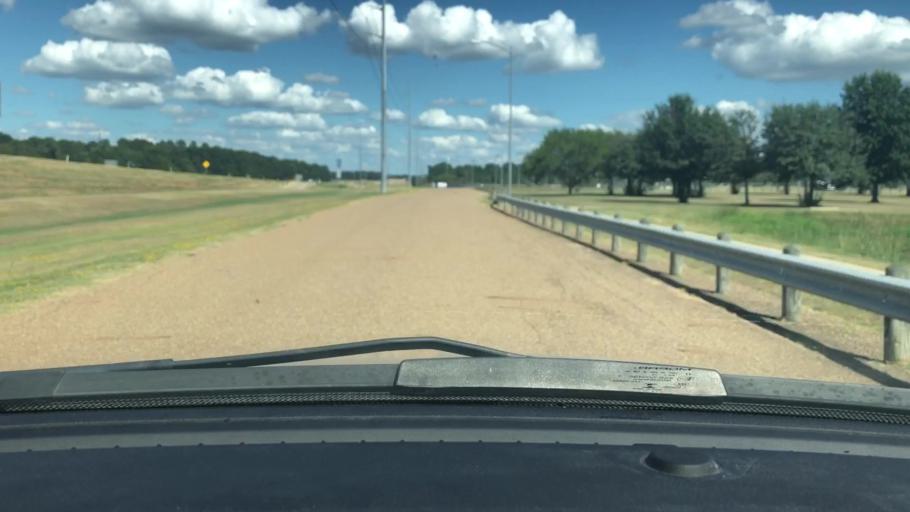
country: US
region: Texas
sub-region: Bowie County
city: Wake Village
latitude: 33.3848
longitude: -94.0897
